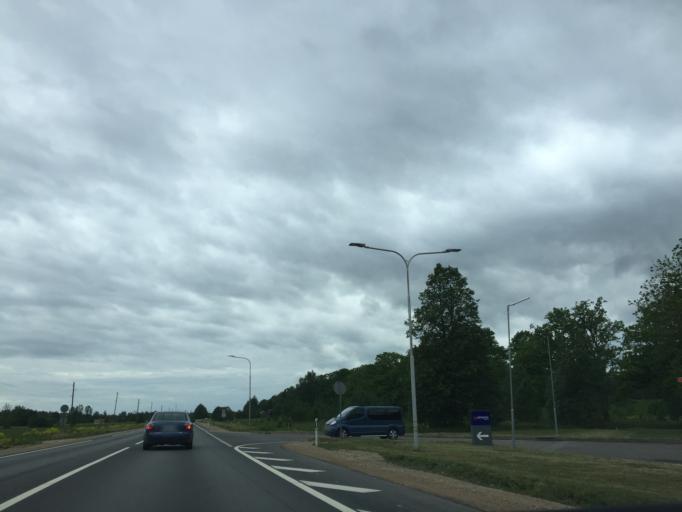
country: LV
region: Plavinu
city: Plavinas
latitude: 56.5992
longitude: 25.6504
